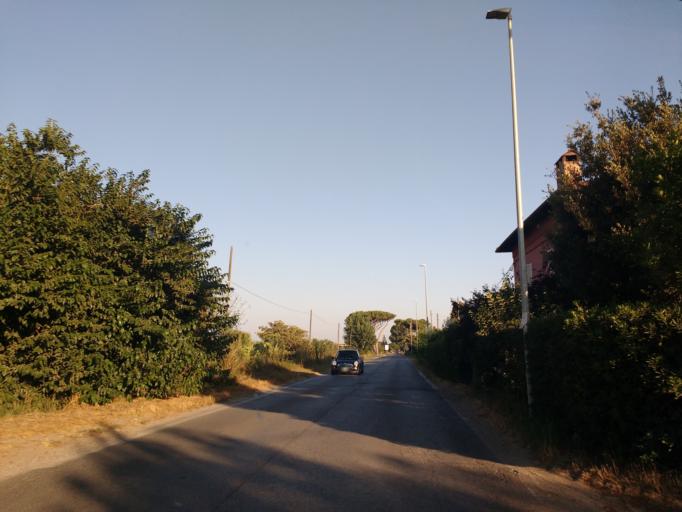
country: IT
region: Latium
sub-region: Citta metropolitana di Roma Capitale
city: Maccarese
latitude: 41.8602
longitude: 12.2129
